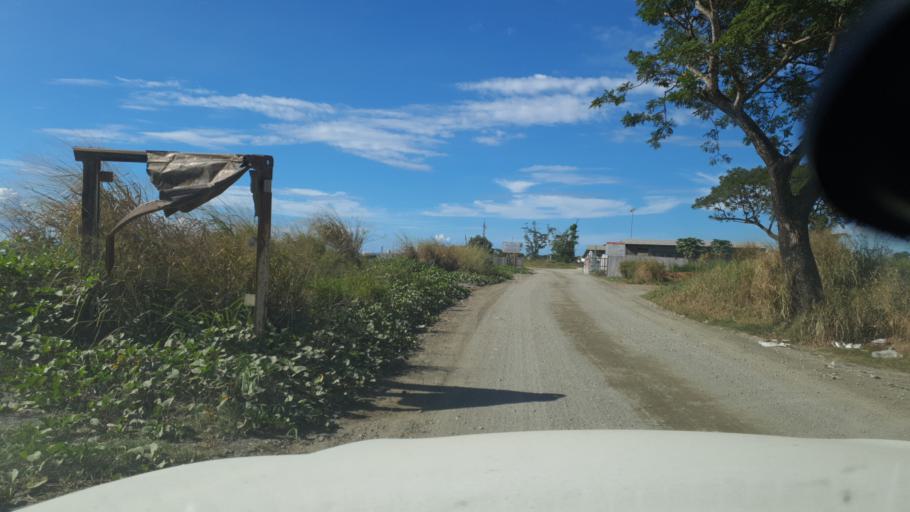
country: SB
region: Guadalcanal
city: Honiara
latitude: -9.4152
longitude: 160.0152
